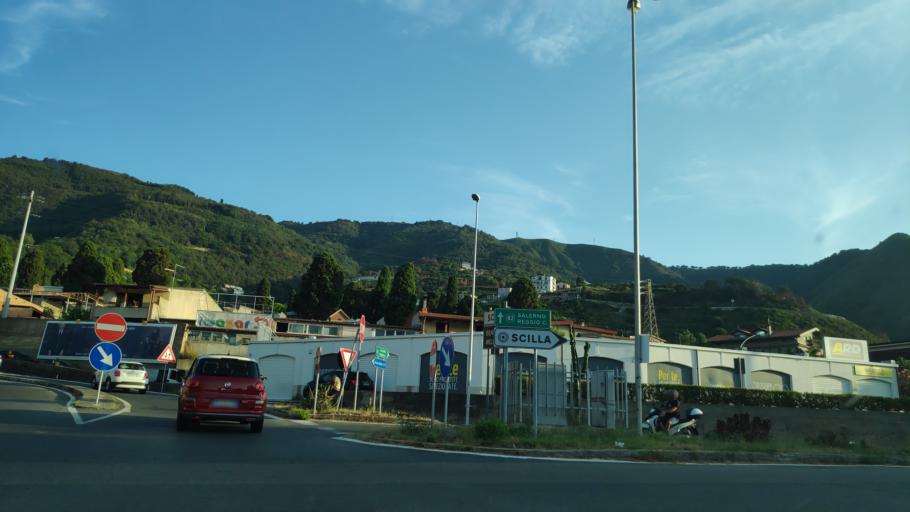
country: IT
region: Calabria
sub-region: Provincia di Reggio Calabria
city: Scilla
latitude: 38.2510
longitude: 15.7204
